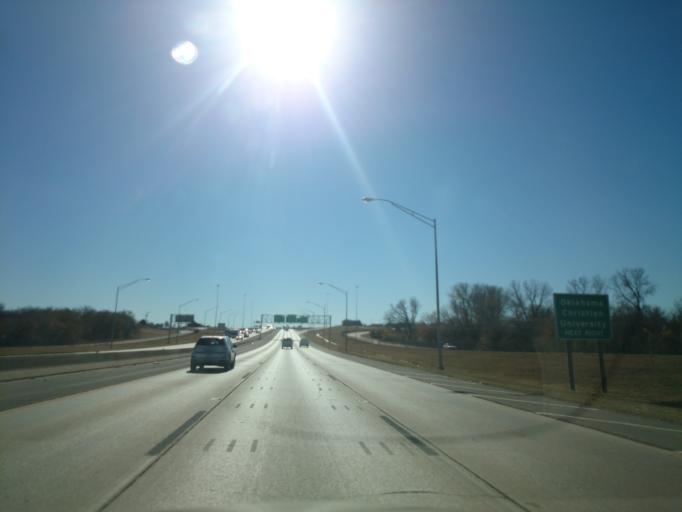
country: US
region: Oklahoma
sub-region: Oklahoma County
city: Edmond
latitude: 35.6179
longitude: -97.4250
